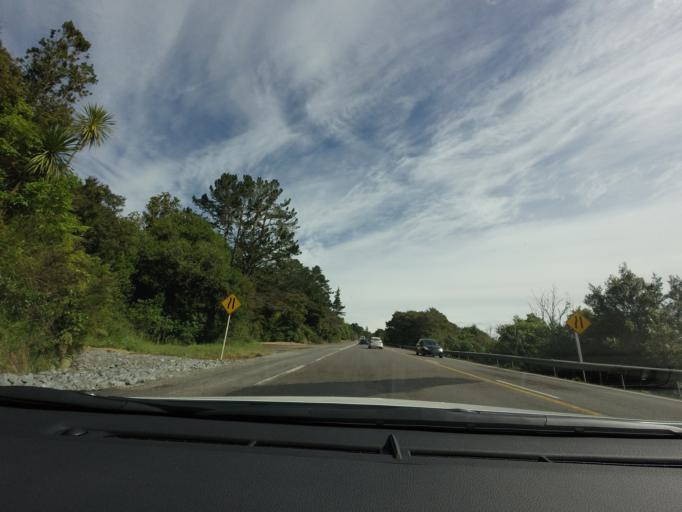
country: NZ
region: Auckland
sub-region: Auckland
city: Warkworth
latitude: -36.4568
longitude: 174.6526
